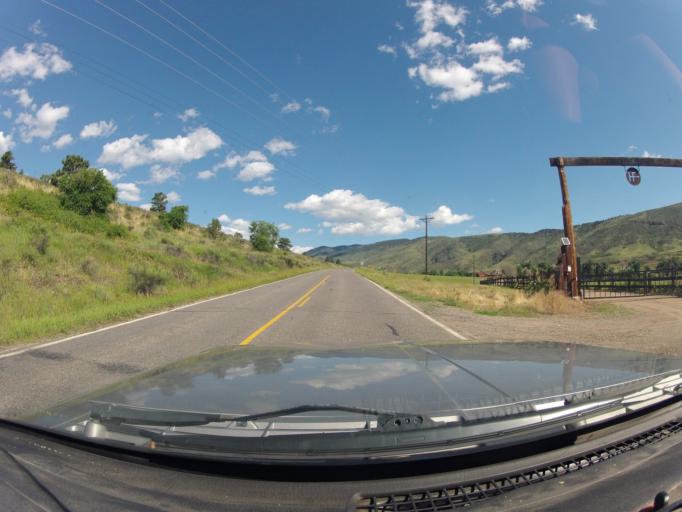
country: US
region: Colorado
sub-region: Larimer County
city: Laporte
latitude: 40.4945
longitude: -105.2222
